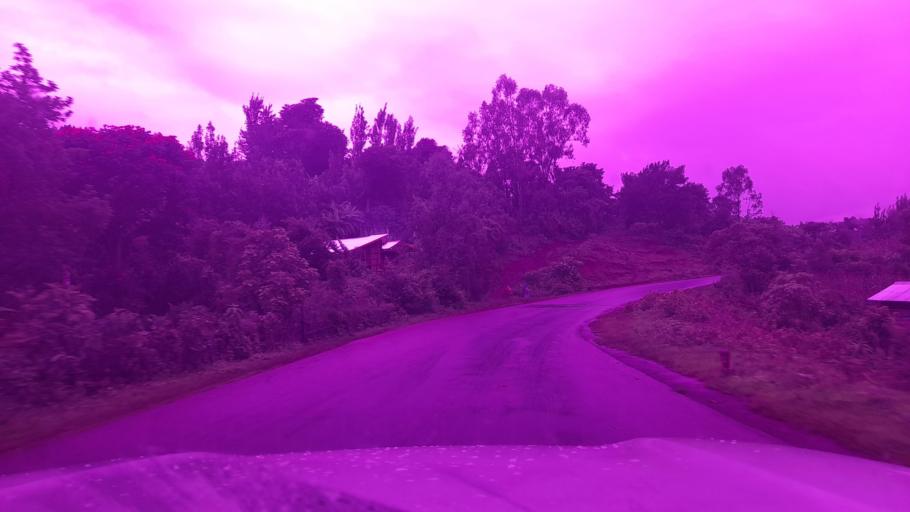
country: ET
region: Oromiya
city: Jima
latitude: 7.8034
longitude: 37.3445
